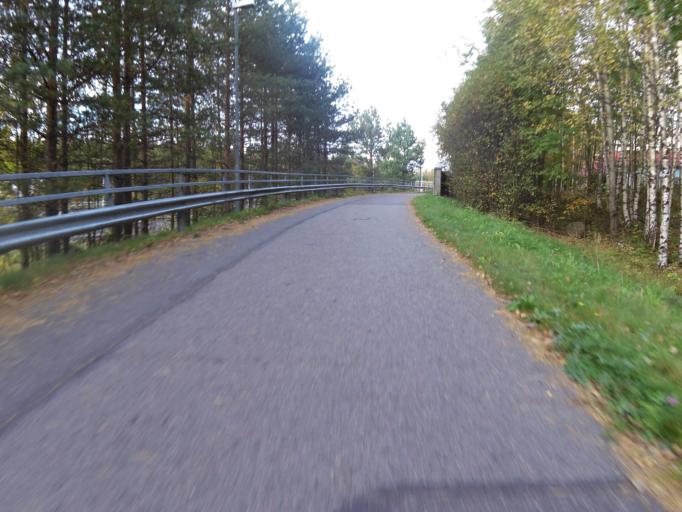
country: FI
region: Uusimaa
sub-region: Helsinki
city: Kauniainen
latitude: 60.2416
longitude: 24.7004
